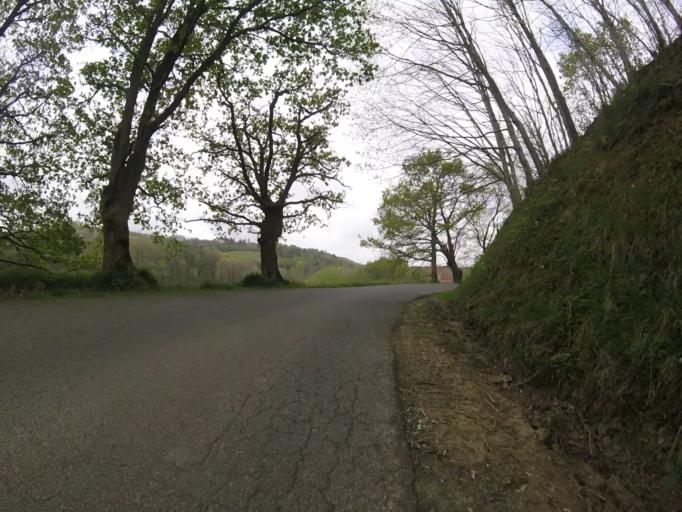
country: ES
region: Basque Country
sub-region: Provincia de Guipuzcoa
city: Zizurkil
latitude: 43.2139
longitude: -2.0852
